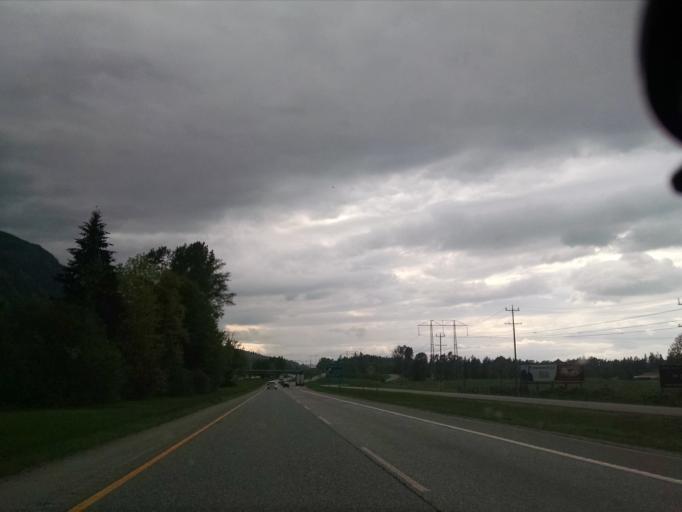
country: CA
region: British Columbia
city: Agassiz
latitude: 49.2023
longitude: -121.7223
